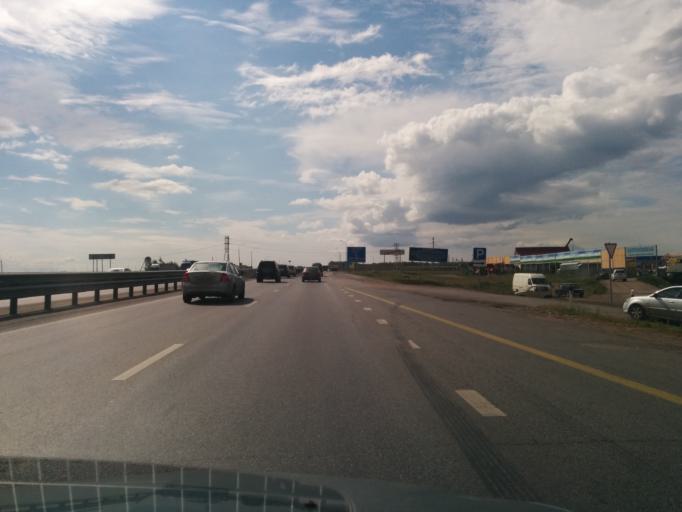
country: RU
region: Bashkortostan
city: Kabakovo
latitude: 54.4988
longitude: 55.9038
